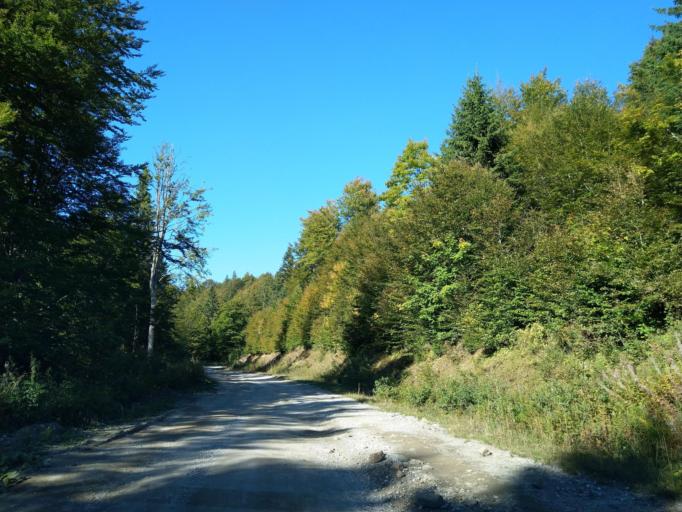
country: RS
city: Sokolovica
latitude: 43.3648
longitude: 20.2588
